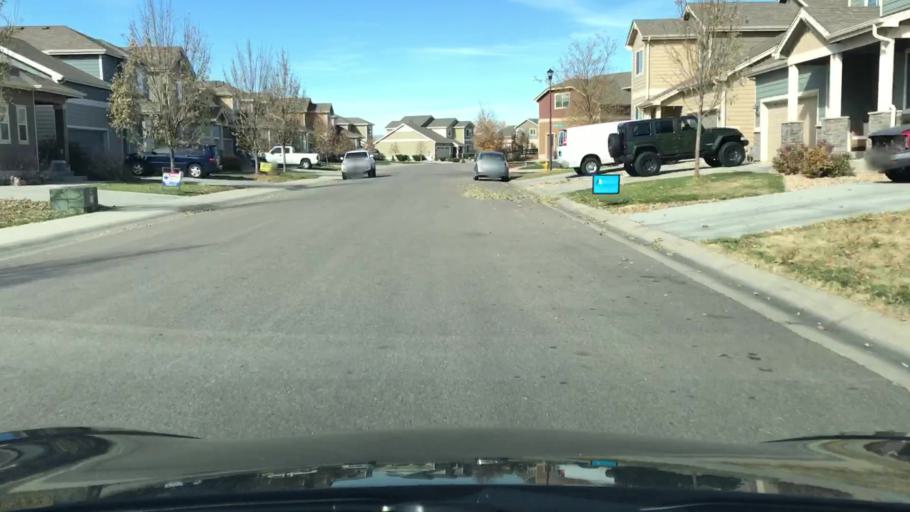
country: US
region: Colorado
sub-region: Larimer County
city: Fort Collins
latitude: 40.5910
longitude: -105.0416
